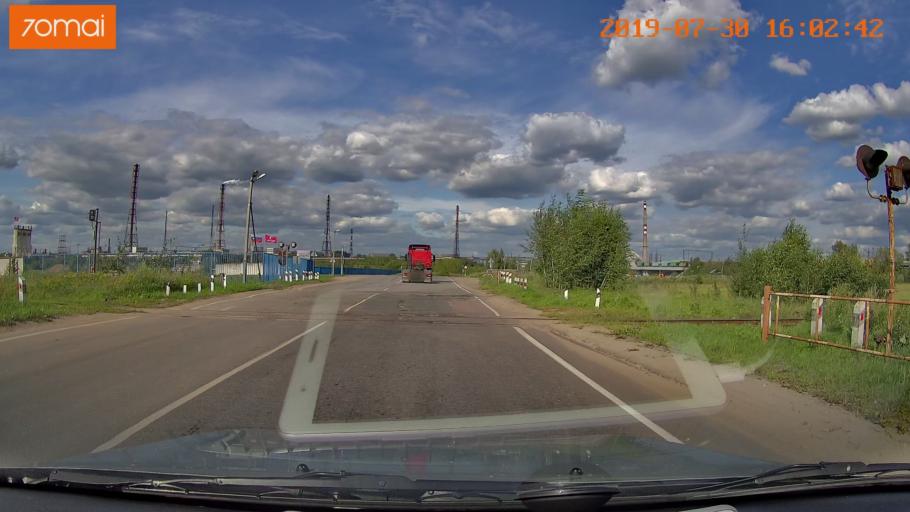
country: RU
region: Moskovskaya
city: Voskresensk
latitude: 55.2889
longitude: 38.6898
